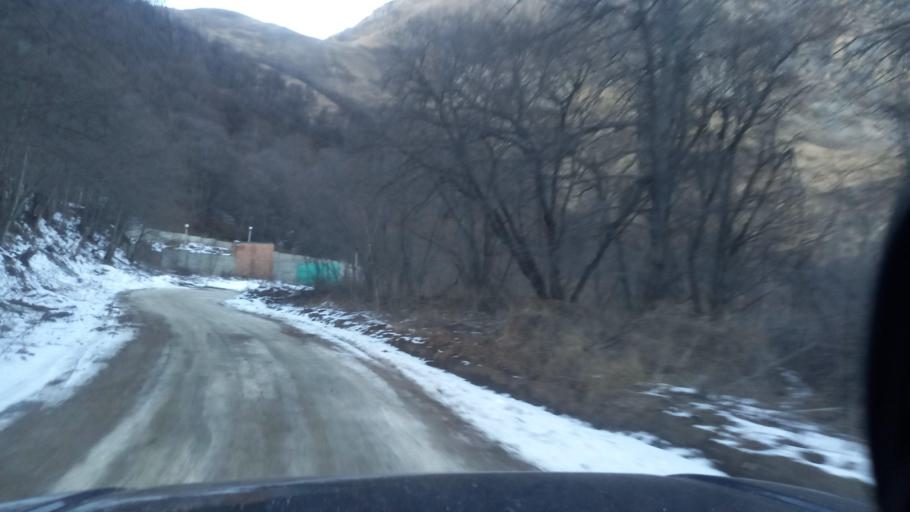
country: RU
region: Ingushetiya
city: Dzhayrakh
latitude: 42.8302
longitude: 44.5736
